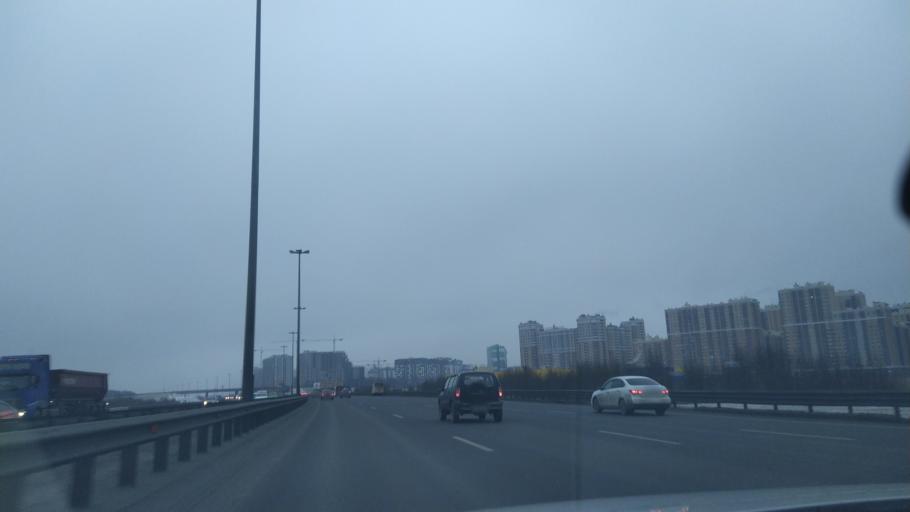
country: RU
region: St.-Petersburg
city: Krasnogvargeisky
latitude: 59.9211
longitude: 30.5271
